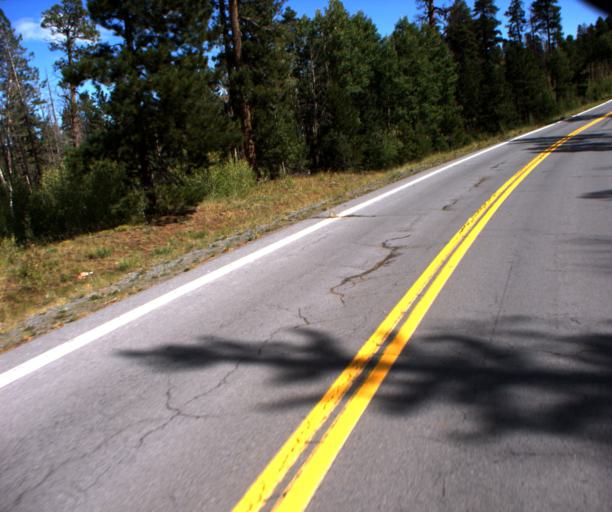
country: US
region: Arizona
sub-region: Apache County
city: Eagar
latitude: 34.0037
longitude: -109.3709
